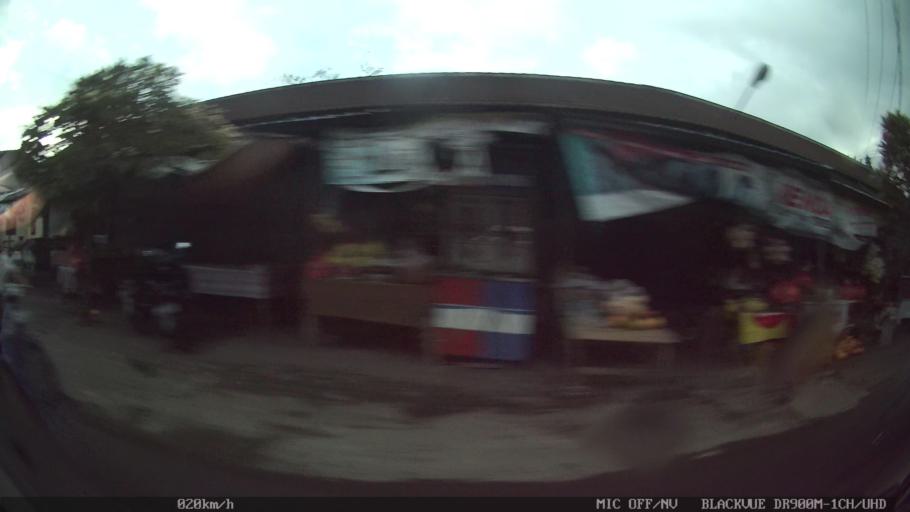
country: ID
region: Bali
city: Banjar Pasekan
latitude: -8.6241
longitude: 115.2744
